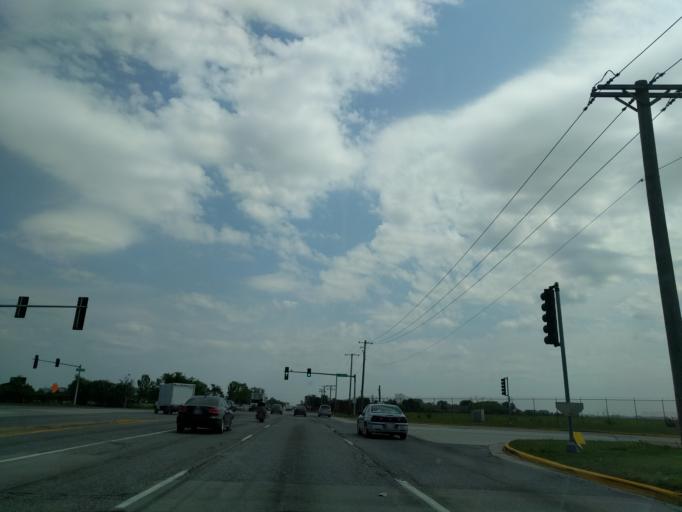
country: US
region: Illinois
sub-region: Cook County
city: Rosemont
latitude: 42.0083
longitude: -87.9234
